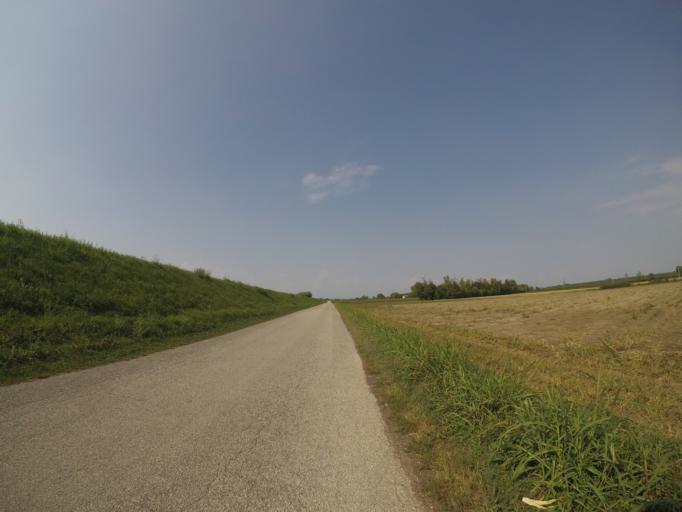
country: IT
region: Friuli Venezia Giulia
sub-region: Provincia di Udine
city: Camino al Tagliamento
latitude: 45.9103
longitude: 12.9311
